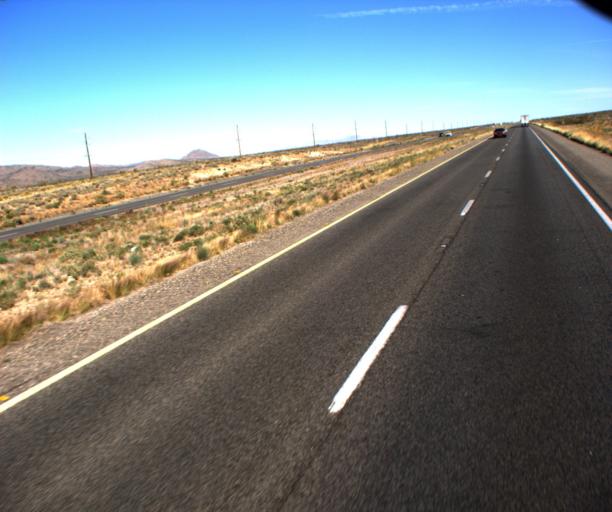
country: US
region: Arizona
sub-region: Mohave County
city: Golden Valley
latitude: 35.3450
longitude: -114.2216
